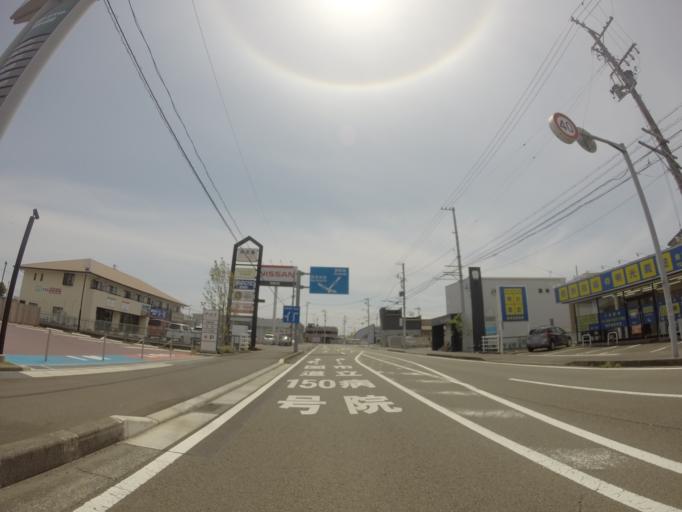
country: JP
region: Shizuoka
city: Yaizu
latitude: 34.8382
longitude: 138.3088
